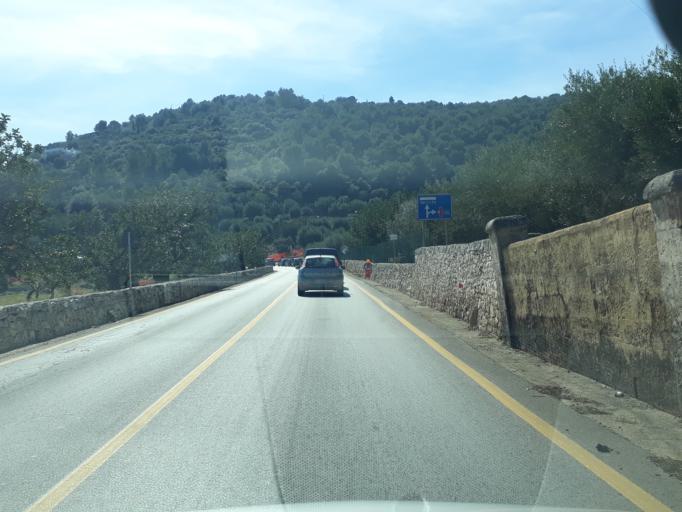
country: IT
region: Apulia
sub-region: Provincia di Brindisi
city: Lamie di Olimpie-Selva
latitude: 40.8172
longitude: 17.3453
